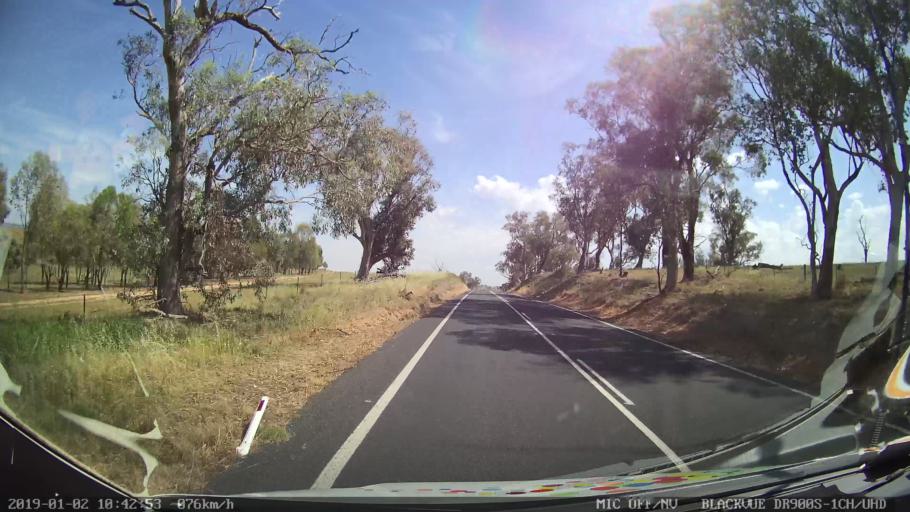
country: AU
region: New South Wales
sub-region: Cootamundra
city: Cootamundra
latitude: -34.7791
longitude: 148.3063
